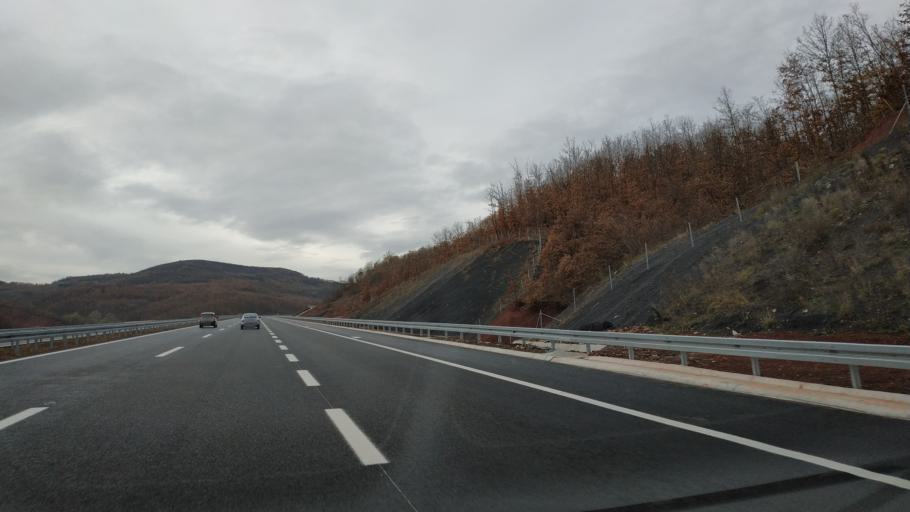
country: RS
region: Central Serbia
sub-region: Nisavski Okrug
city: Gadzin Han
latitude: 43.2563
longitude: 22.1554
